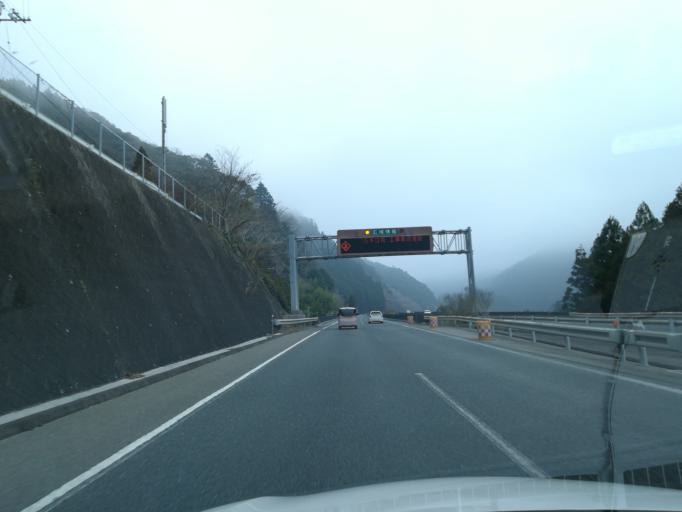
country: JP
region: Ehime
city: Kawanoecho
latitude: 33.7802
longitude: 133.6611
